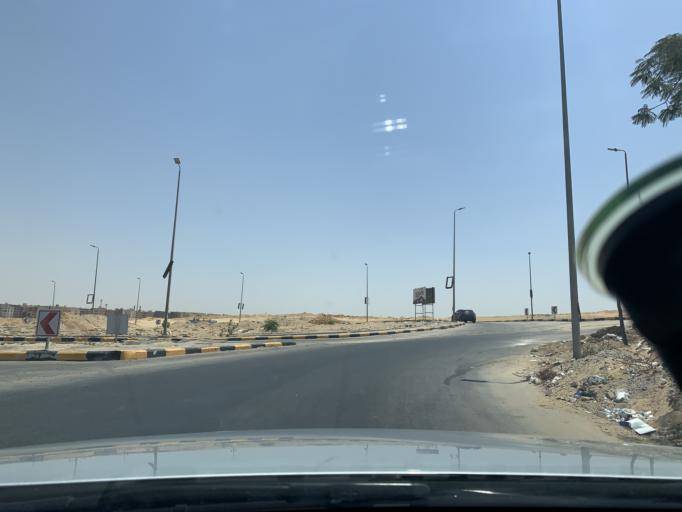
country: EG
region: Muhafazat al Qahirah
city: Cairo
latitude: 30.0001
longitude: 31.4627
